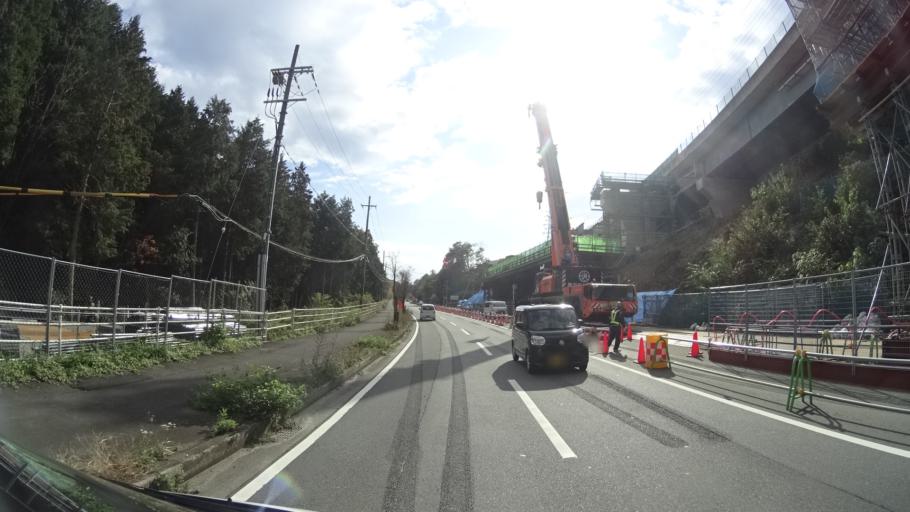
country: JP
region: Kyoto
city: Fukuchiyama
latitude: 35.2927
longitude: 135.1778
